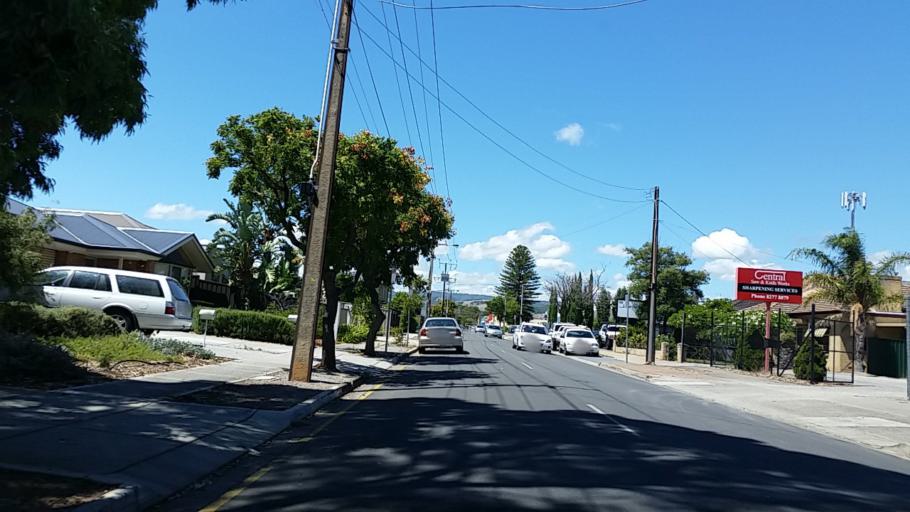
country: AU
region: South Australia
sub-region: Marion
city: Clovelly Park
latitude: -34.9867
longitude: 138.5682
